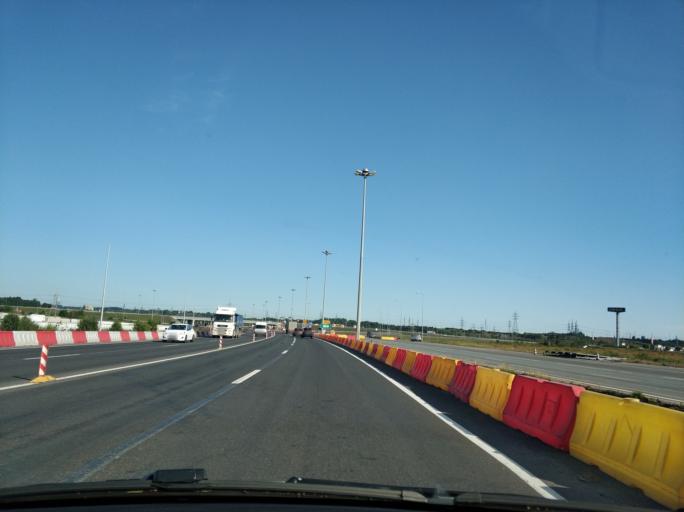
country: RU
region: Leningrad
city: Bugry
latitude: 60.0877
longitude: 30.3750
